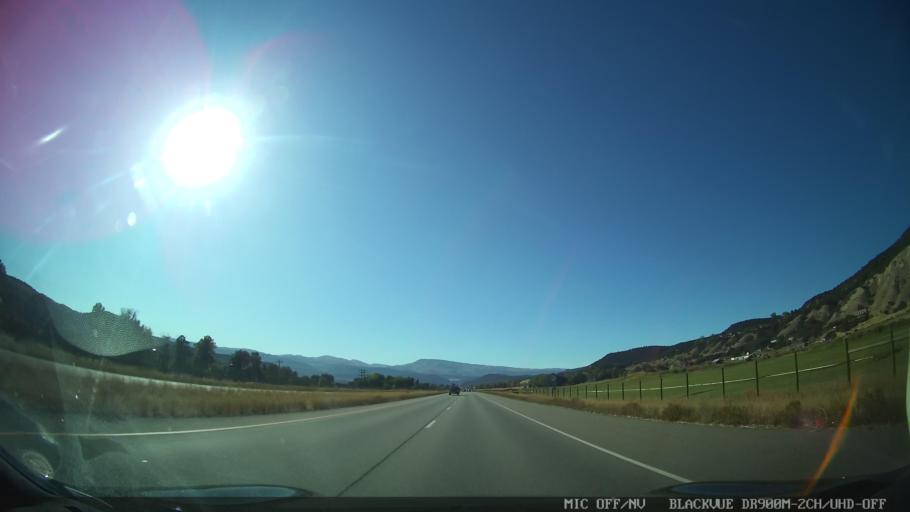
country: US
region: Colorado
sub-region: Eagle County
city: El Jebel
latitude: 39.4069
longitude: -107.1419
